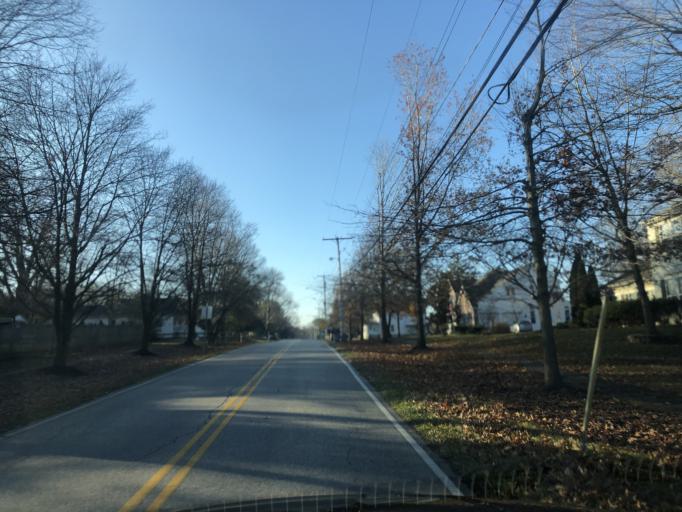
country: US
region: Maryland
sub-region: Anne Arundel County
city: Odenton
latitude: 39.0822
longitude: -76.7066
